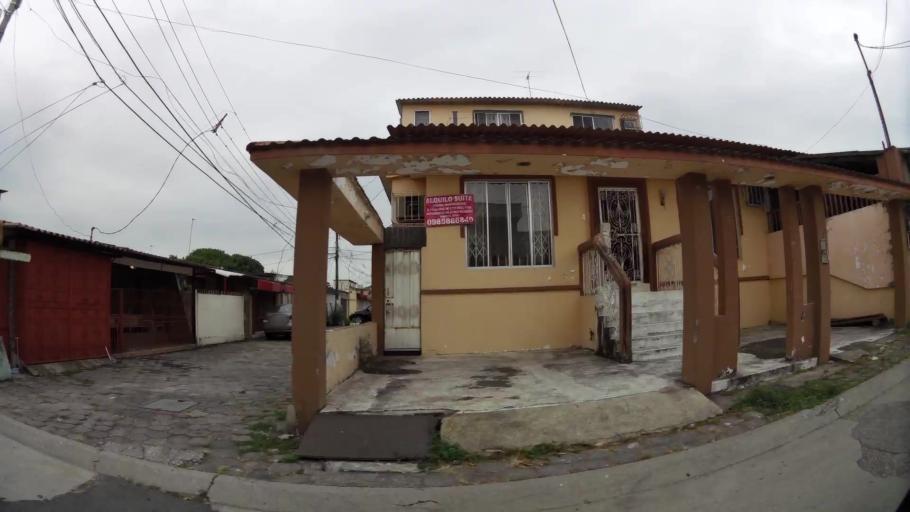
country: EC
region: Guayas
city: Eloy Alfaro
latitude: -2.1421
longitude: -79.9072
